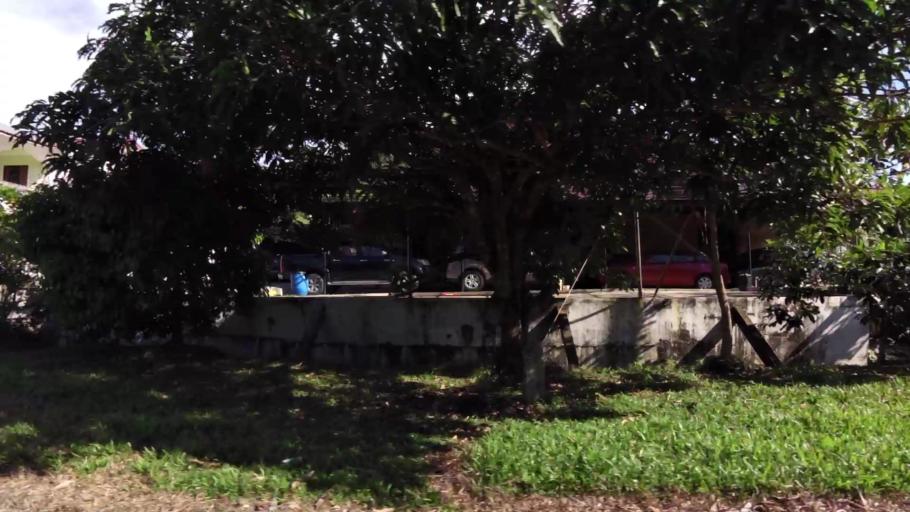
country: BN
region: Brunei and Muara
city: Bandar Seri Begawan
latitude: 4.9804
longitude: 114.9624
